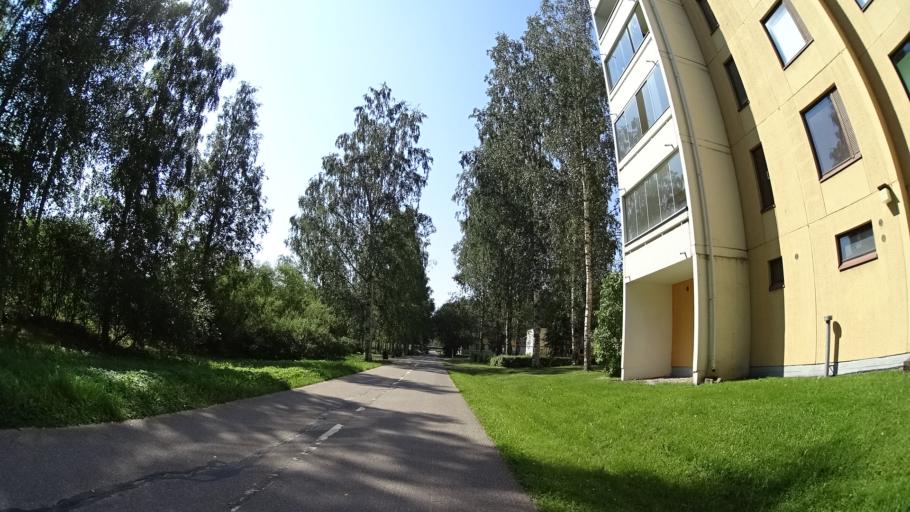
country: FI
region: Uusimaa
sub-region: Helsinki
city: Kerava
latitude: 60.3921
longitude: 25.0943
